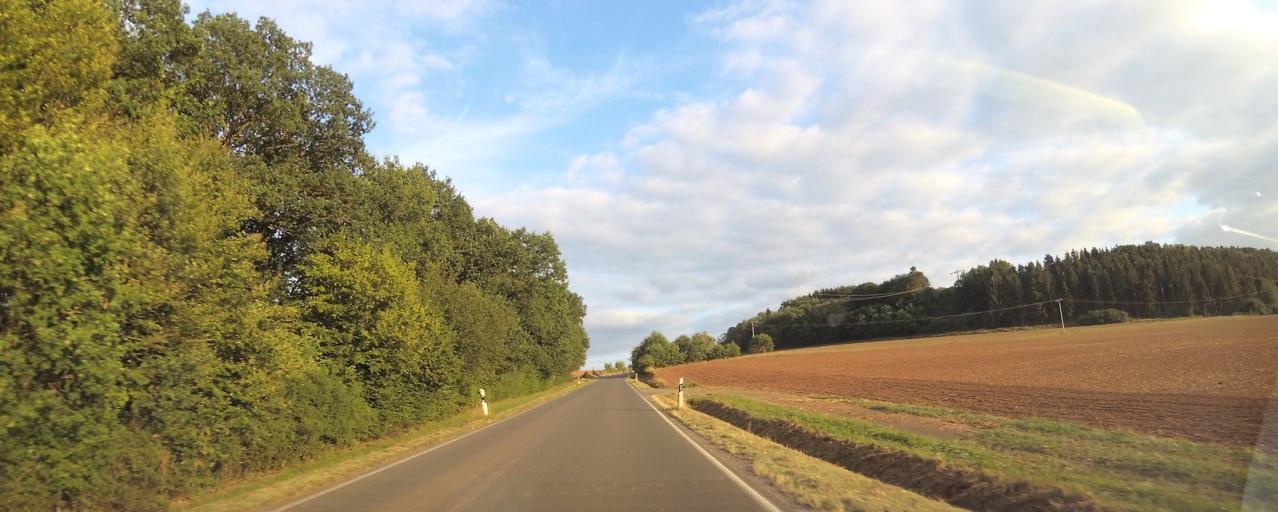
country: DE
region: Rheinland-Pfalz
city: Beilingen
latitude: 49.9662
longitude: 6.6635
